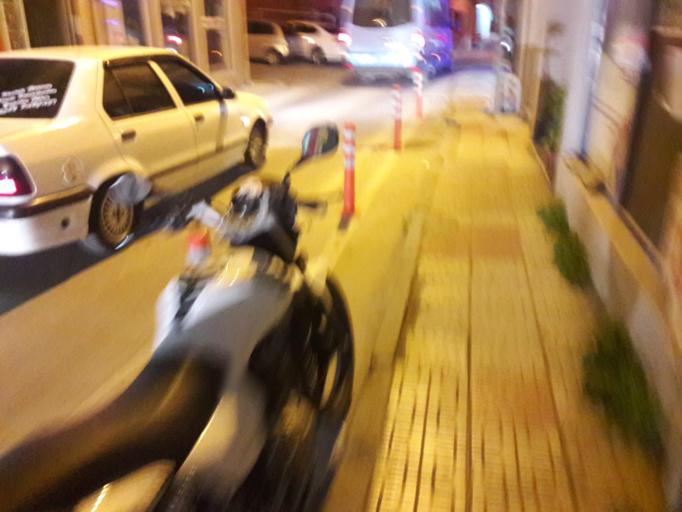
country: TR
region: Sinop
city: Sinop
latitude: 42.0250
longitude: 35.1479
